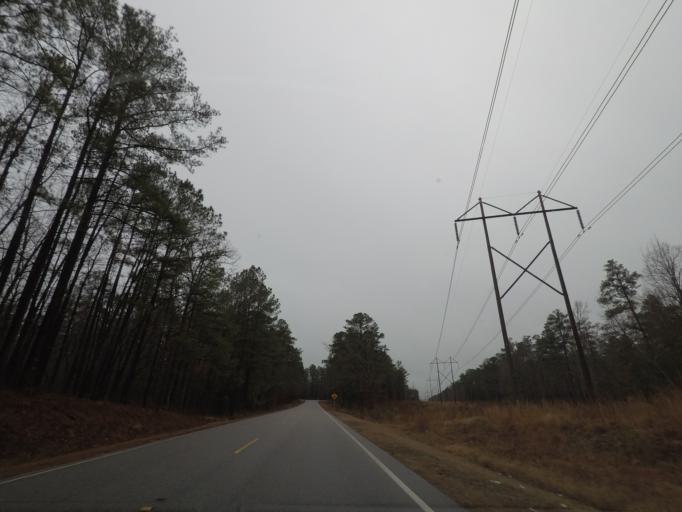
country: US
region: North Carolina
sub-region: Cumberland County
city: Spring Lake
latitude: 35.2598
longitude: -78.9923
